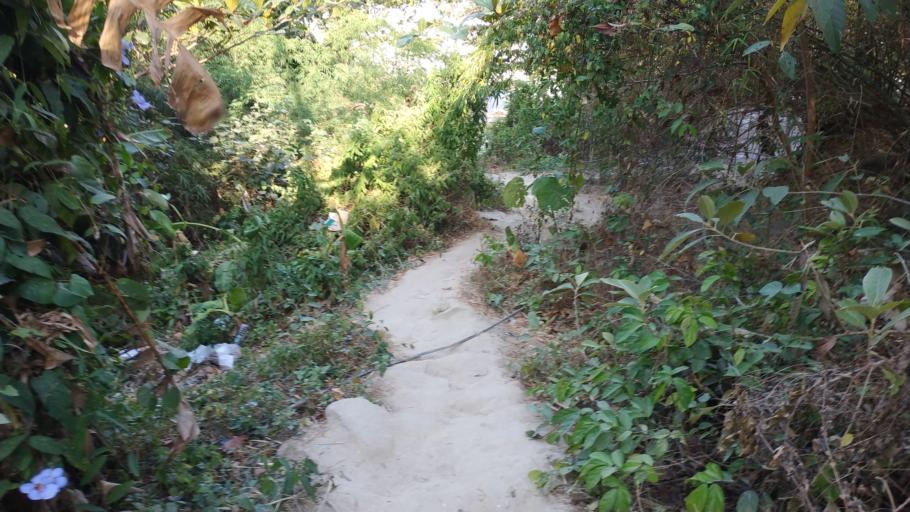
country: TH
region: Phuket
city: Patong
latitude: 7.8741
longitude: 98.2760
